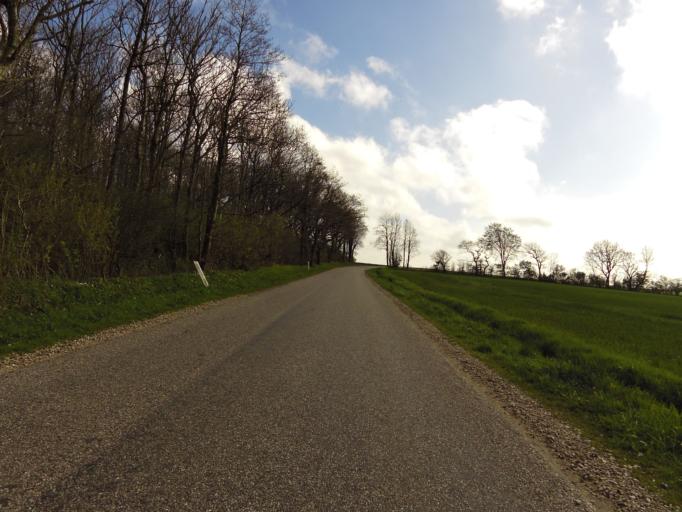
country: DK
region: South Denmark
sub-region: Vejen Kommune
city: Rodding
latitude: 55.3441
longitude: 8.9895
